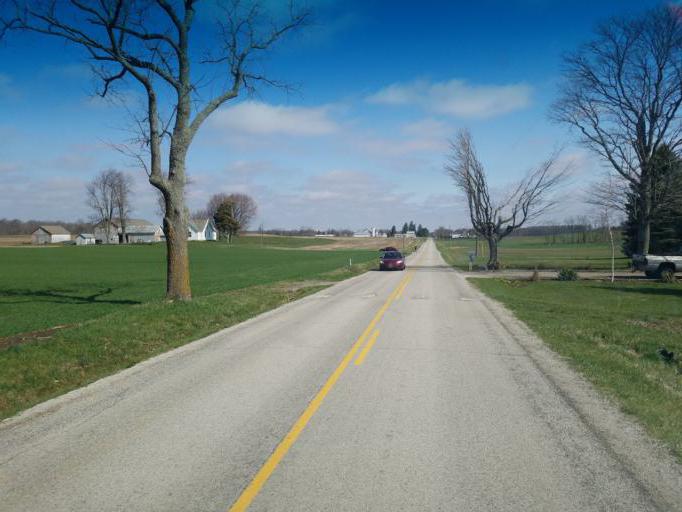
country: US
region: Ohio
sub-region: Crawford County
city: Bucyrus
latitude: 40.8582
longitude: -82.8730
